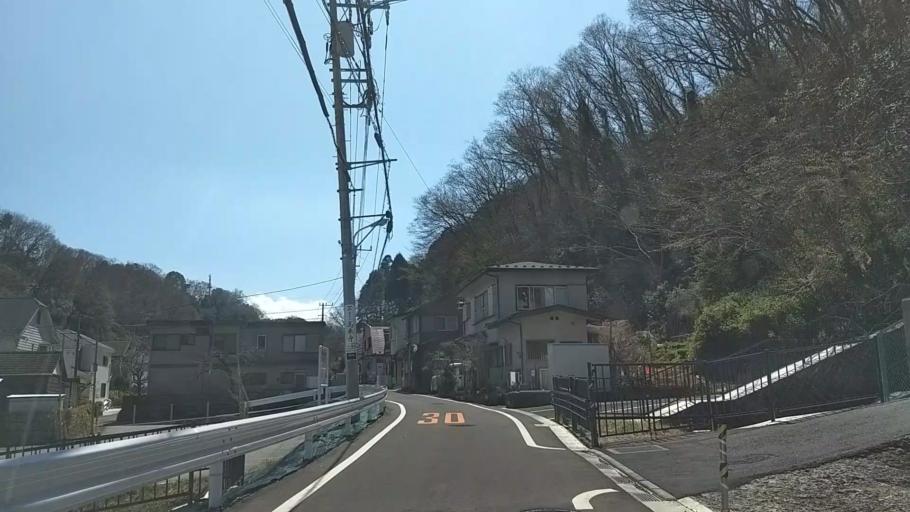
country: JP
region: Tokyo
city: Hachioji
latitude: 35.6366
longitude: 139.2766
